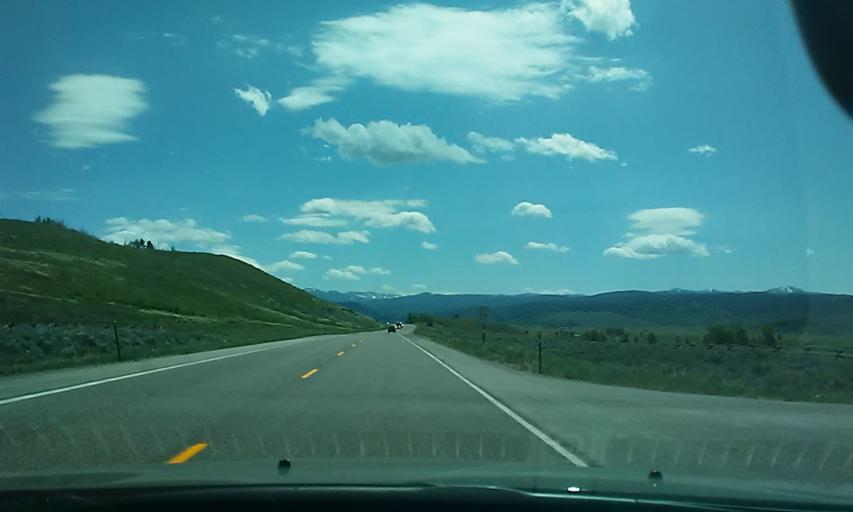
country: US
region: Wyoming
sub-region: Teton County
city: Jackson
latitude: 43.8398
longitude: -110.4539
